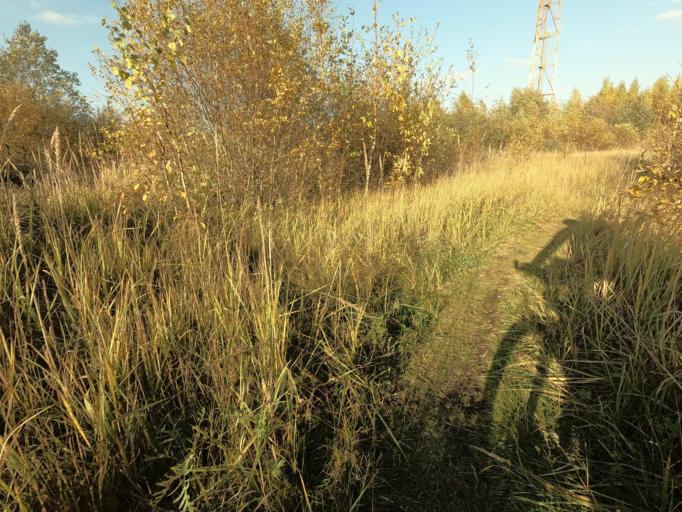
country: RU
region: Leningrad
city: Mga
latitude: 59.7457
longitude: 31.0614
